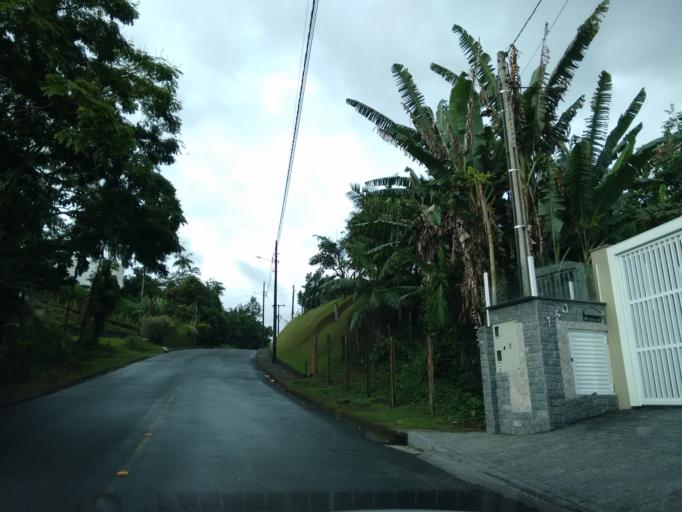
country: BR
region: Santa Catarina
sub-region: Pomerode
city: Pomerode
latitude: -26.7308
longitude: -49.1700
